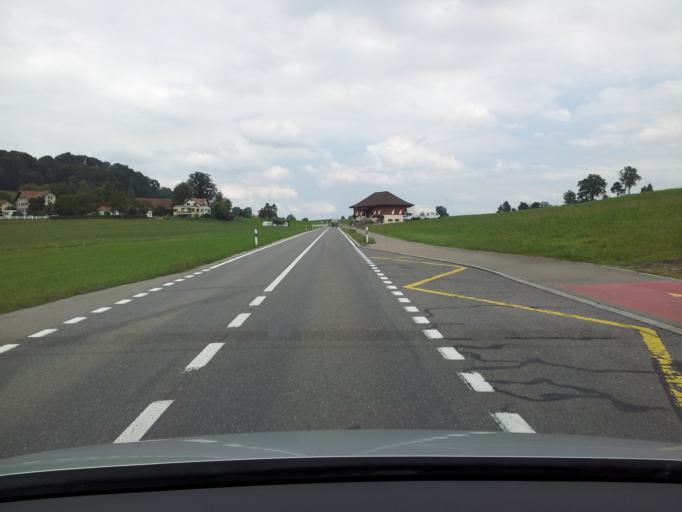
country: CH
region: Lucerne
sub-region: Sursee District
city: Buttisholz
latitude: 47.1193
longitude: 8.1043
